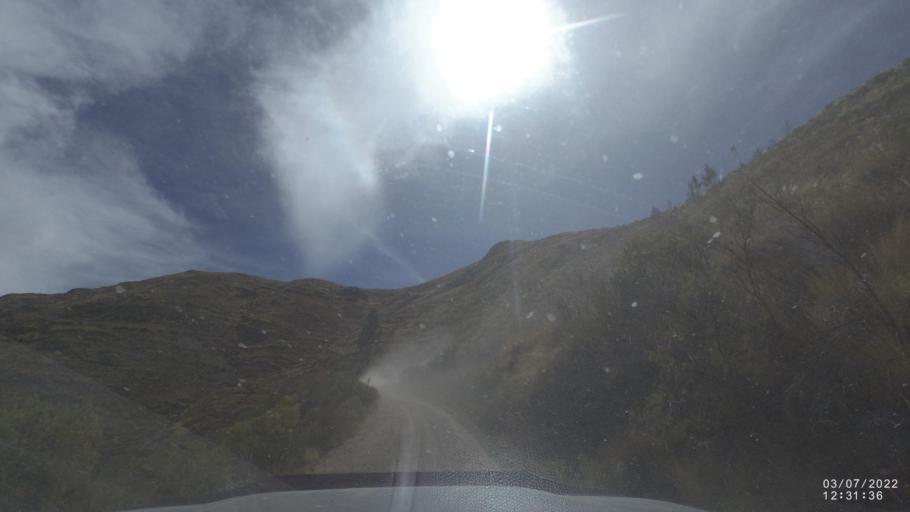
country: BO
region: Cochabamba
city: Irpa Irpa
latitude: -17.8093
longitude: -66.6067
